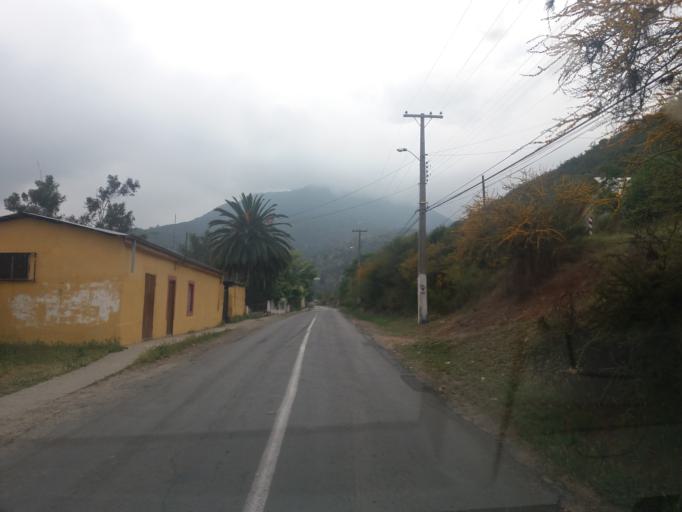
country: CL
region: Valparaiso
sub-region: Provincia de Marga Marga
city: Limache
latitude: -33.0522
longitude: -71.1043
